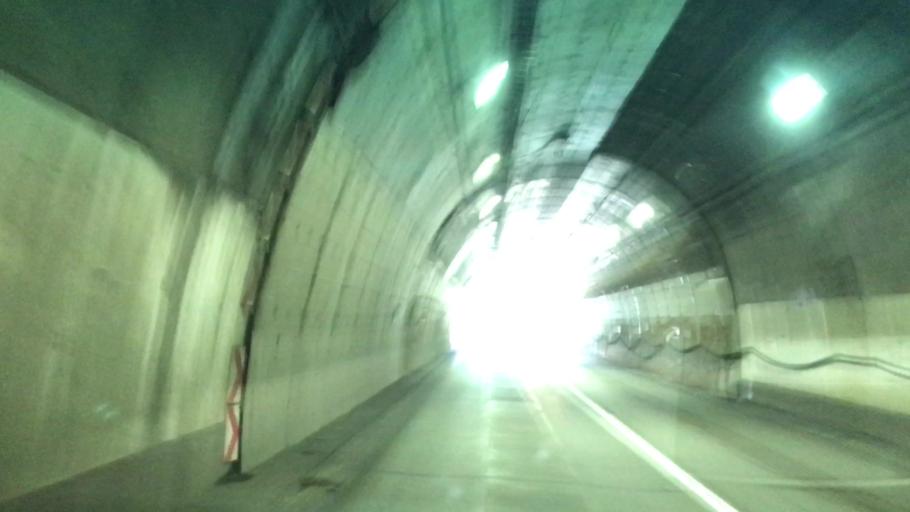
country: JP
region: Hokkaido
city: Yoichi
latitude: 43.0512
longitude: 140.6820
